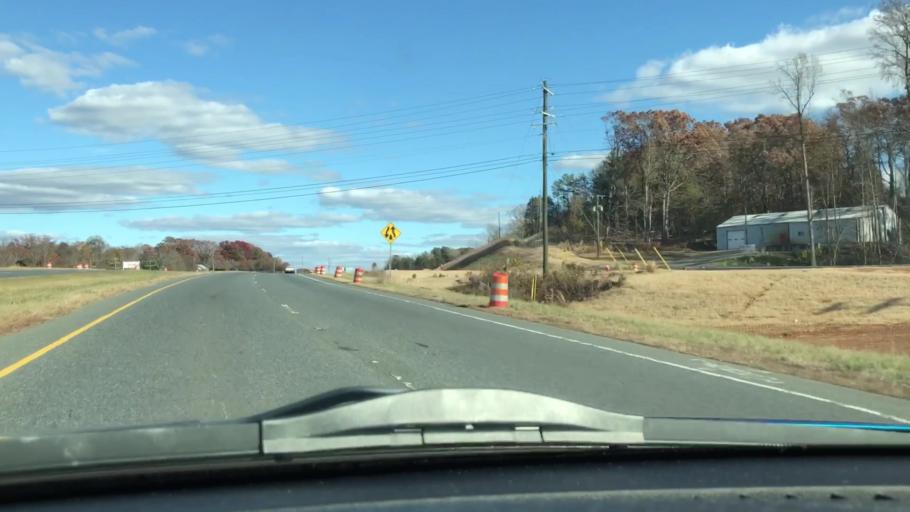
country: US
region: North Carolina
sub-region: Randolph County
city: Franklinville
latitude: 35.7237
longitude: -79.7512
